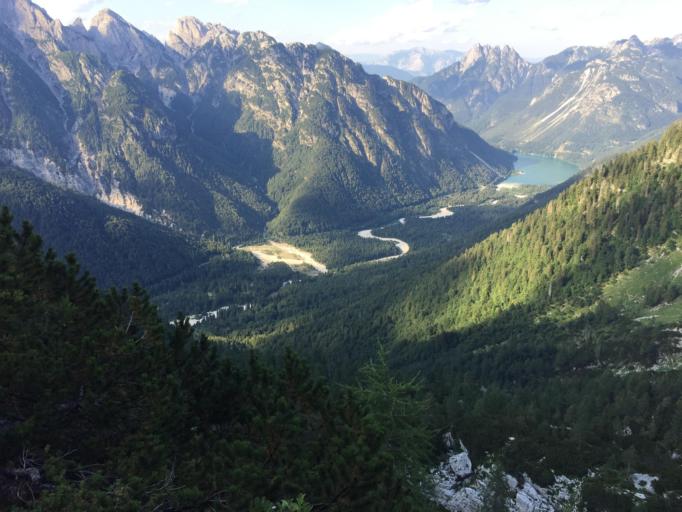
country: SI
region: Bovec
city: Bovec
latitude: 46.3880
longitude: 13.5306
